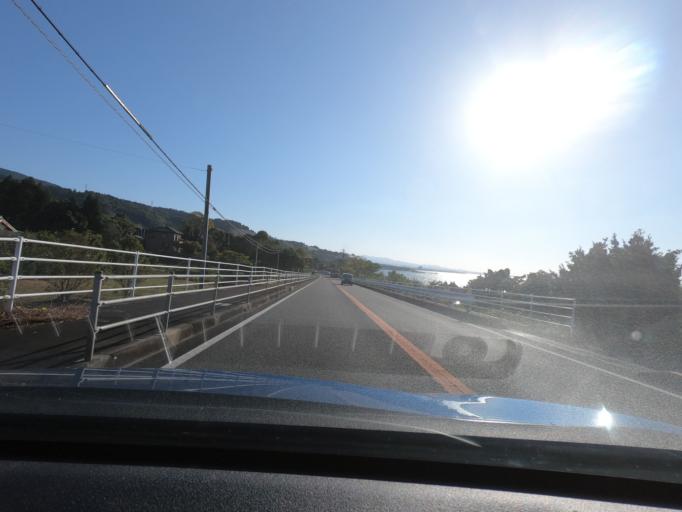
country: JP
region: Kumamoto
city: Minamata
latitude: 32.1573
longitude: 130.3638
